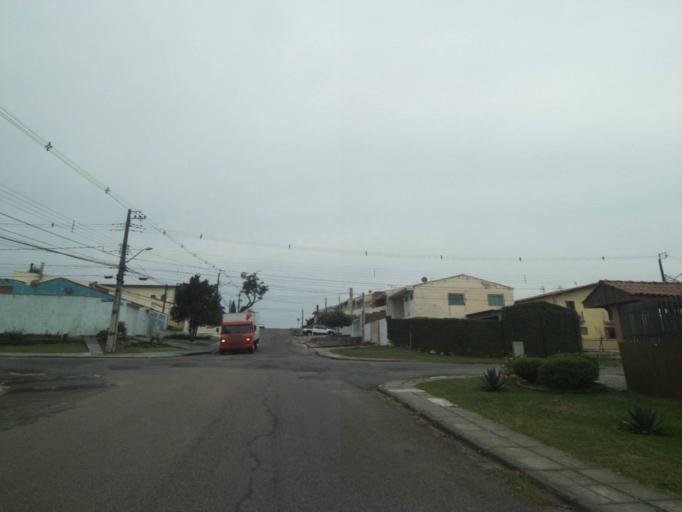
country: BR
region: Parana
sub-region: Pinhais
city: Pinhais
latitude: -25.3948
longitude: -49.2004
